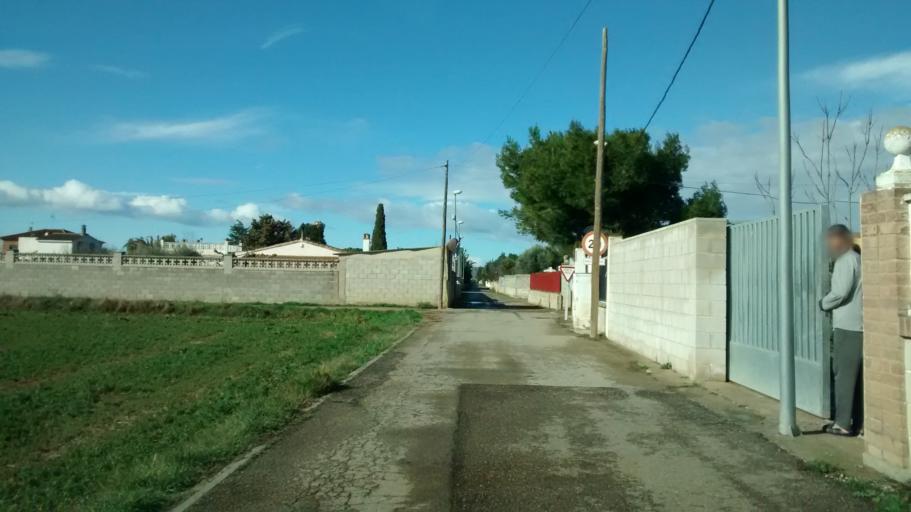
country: ES
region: Aragon
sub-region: Provincia de Zaragoza
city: Villanueva de Gallego
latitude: 41.7346
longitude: -0.8001
